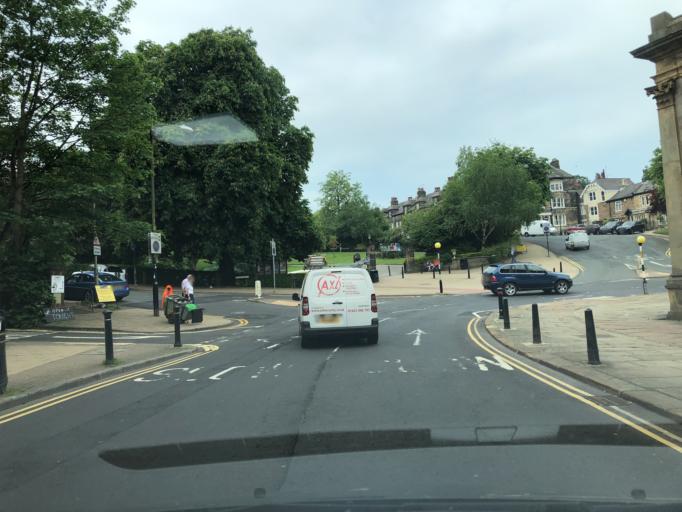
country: GB
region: England
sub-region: North Yorkshire
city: Harrogate
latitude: 53.9934
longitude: -1.5466
